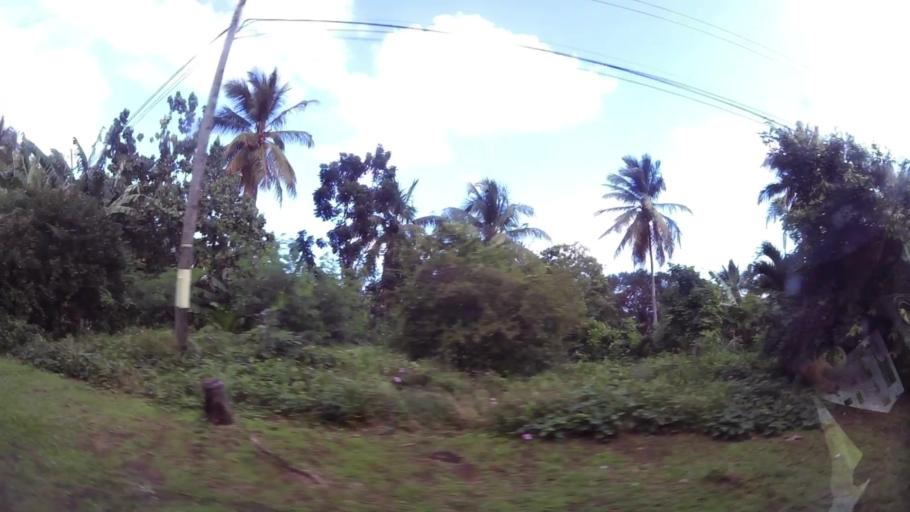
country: DM
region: Saint Andrew
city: Marigot
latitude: 15.4994
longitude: -61.2647
